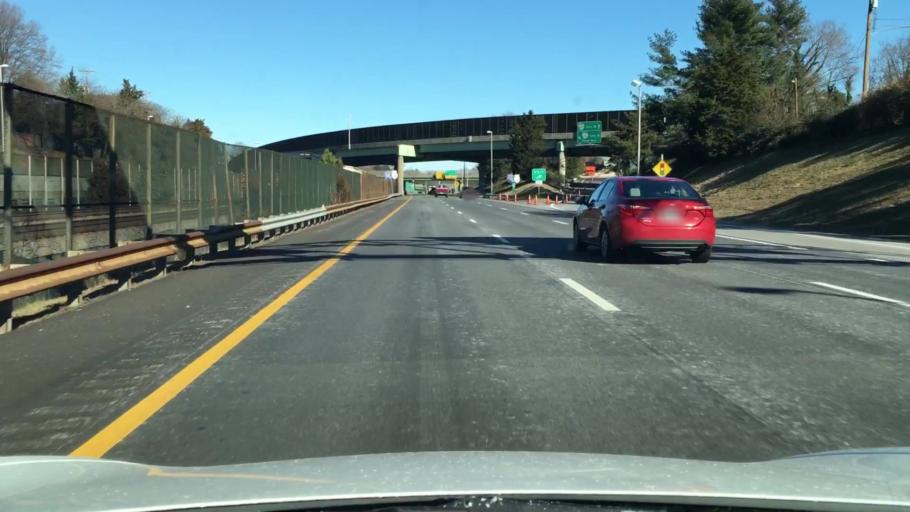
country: US
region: Virginia
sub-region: City of Richmond
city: Richmond
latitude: 37.5528
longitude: -77.4905
